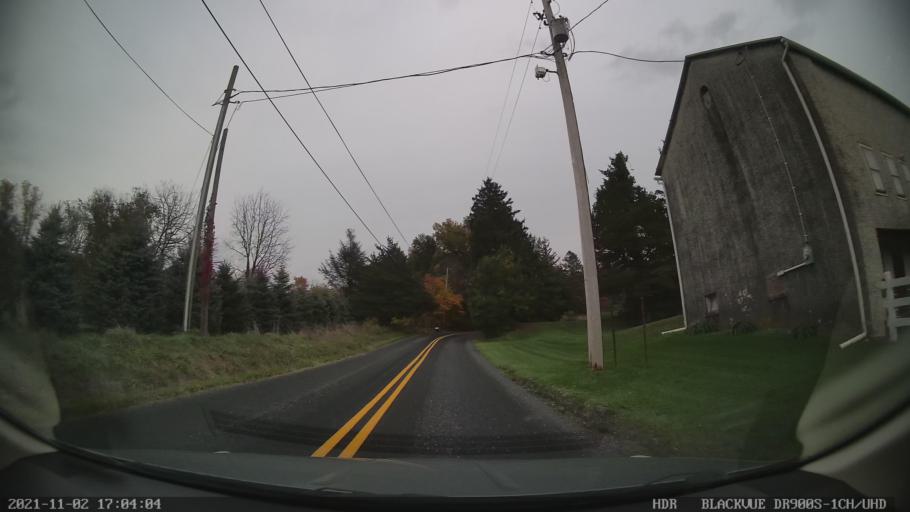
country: US
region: Pennsylvania
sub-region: Berks County
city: Fleetwood
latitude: 40.4403
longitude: -75.8390
